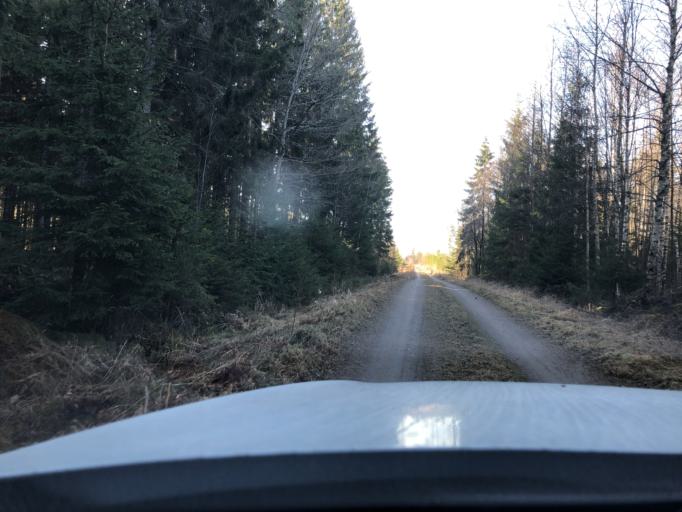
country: SE
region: Gaevleborg
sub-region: Gavle Kommun
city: Hedesunda
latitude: 60.3045
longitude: 16.8961
